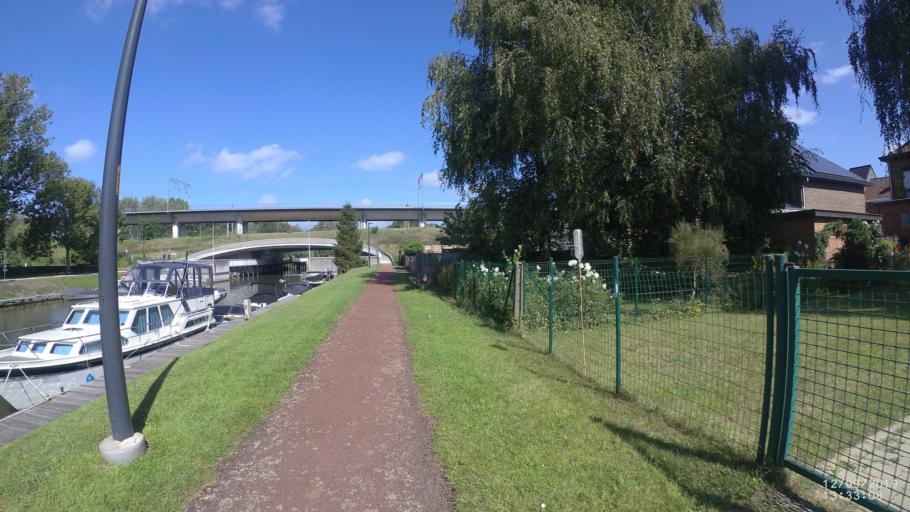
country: BE
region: Flanders
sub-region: Provincie Oost-Vlaanderen
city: Gent
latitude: 51.0385
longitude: 3.6906
